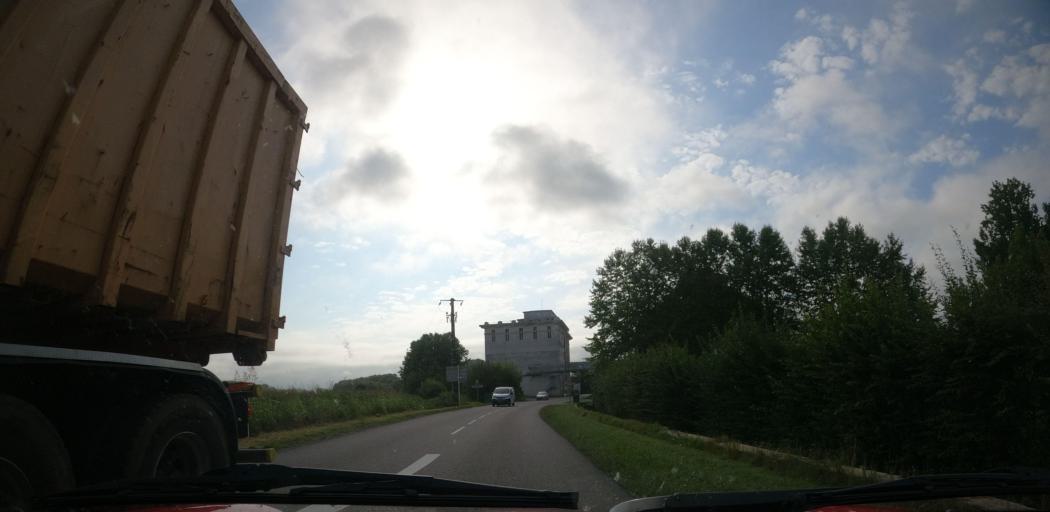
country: FR
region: Aquitaine
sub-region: Departement des Landes
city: Peyrehorade
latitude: 43.5427
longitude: -1.0969
